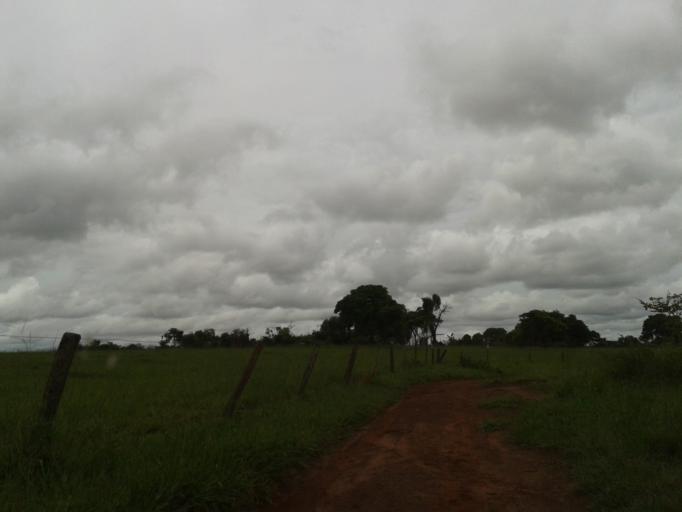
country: BR
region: Minas Gerais
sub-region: Capinopolis
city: Capinopolis
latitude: -18.7855
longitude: -49.7875
